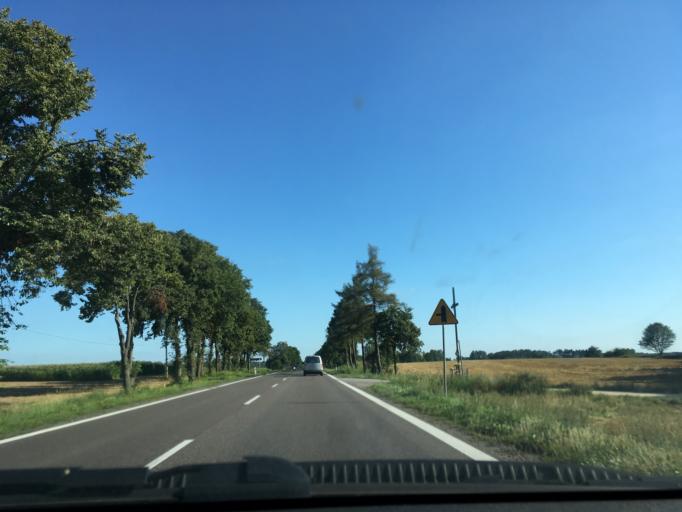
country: PL
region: Podlasie
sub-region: Powiat sokolski
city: Janow
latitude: 53.4249
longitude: 23.1078
